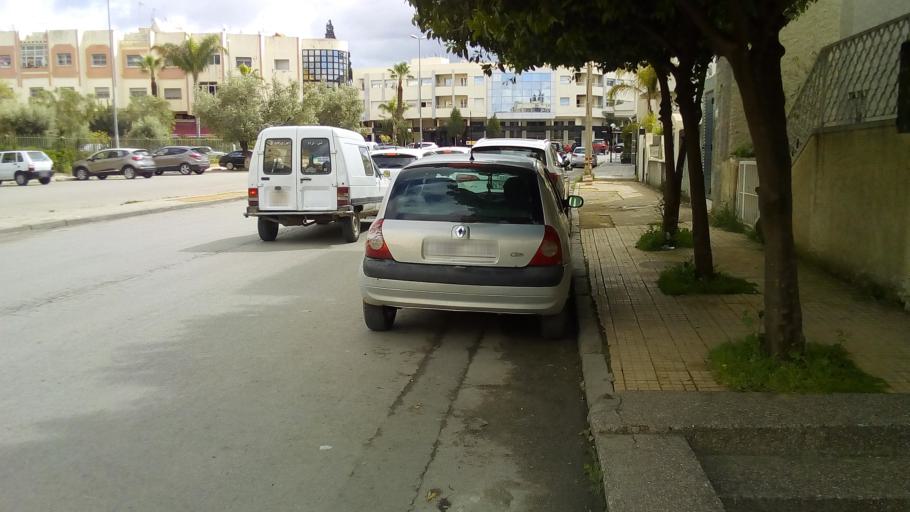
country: MA
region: Fes-Boulemane
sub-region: Fes
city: Fes
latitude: 34.0191
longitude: -5.0064
